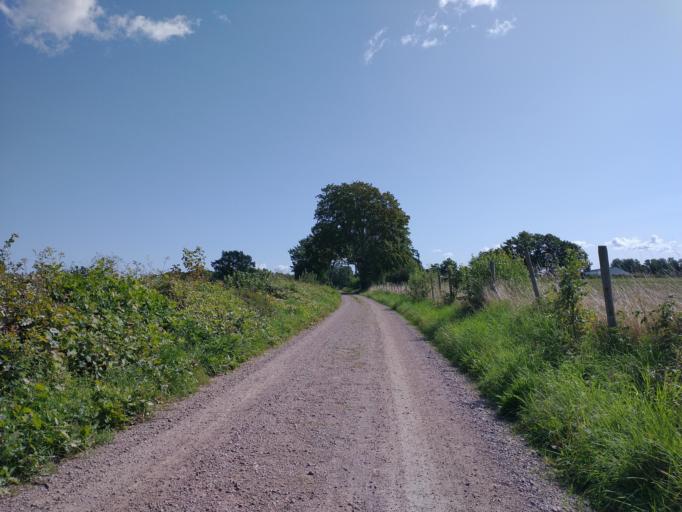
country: SE
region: Kalmar
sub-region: Kalmar Kommun
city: Lindsdal
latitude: 56.7919
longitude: 16.2941
